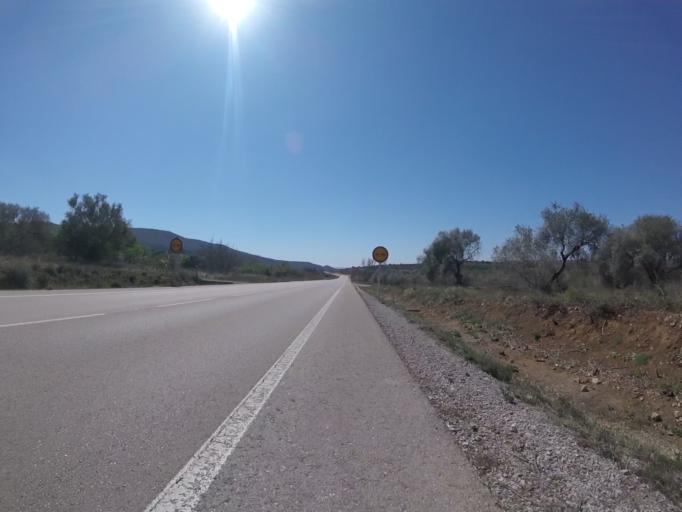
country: ES
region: Valencia
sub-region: Provincia de Castello
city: Cuevas de Vinroma
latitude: 40.3832
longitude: 0.1459
